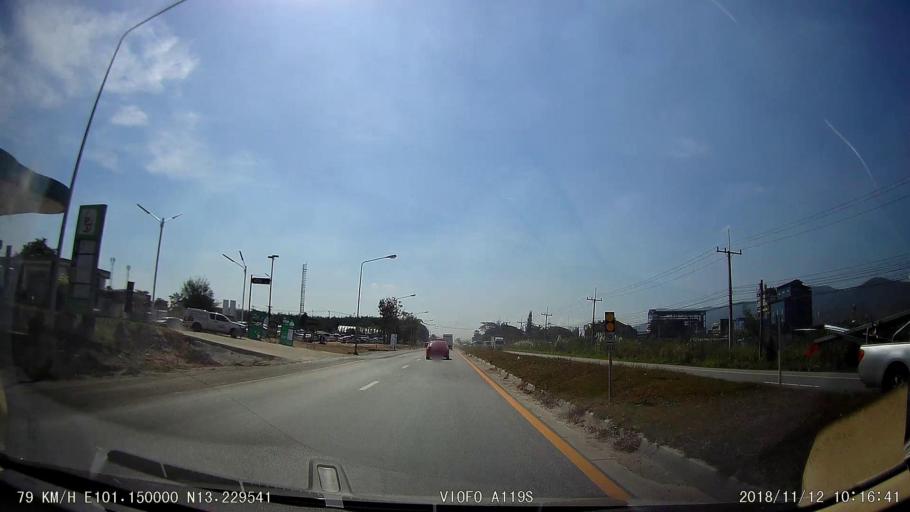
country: TH
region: Chon Buri
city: Ban Bueng
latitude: 13.2290
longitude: 101.1502
